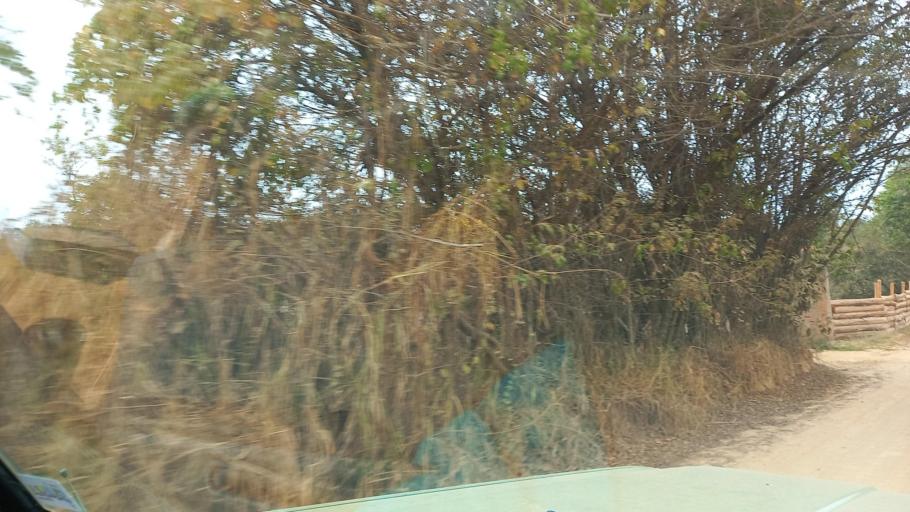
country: BR
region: Sao Paulo
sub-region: Moji-Guacu
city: Mogi-Gaucu
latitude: -22.2968
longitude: -46.8325
